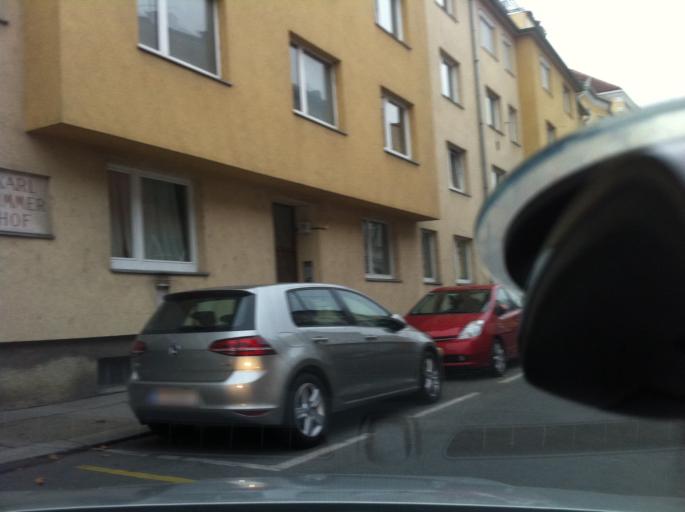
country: AT
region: Vienna
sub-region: Wien Stadt
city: Vienna
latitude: 48.1896
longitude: 16.3101
